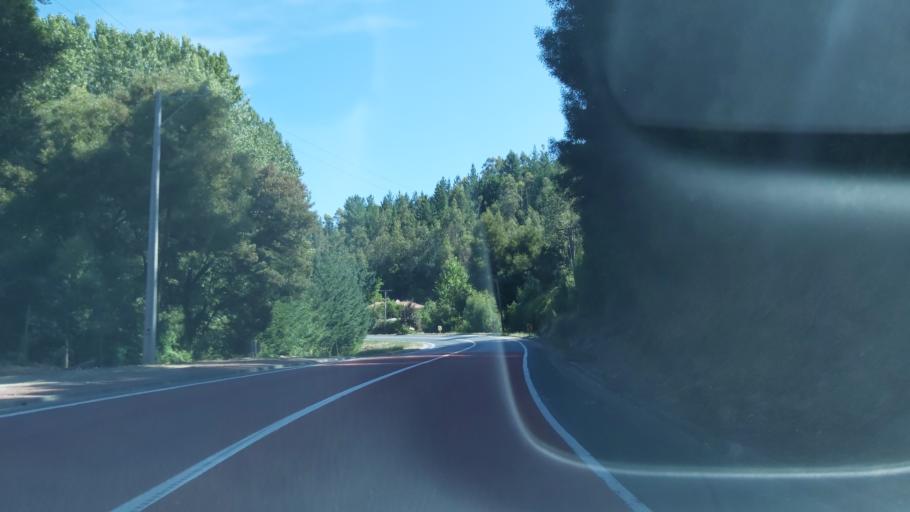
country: CL
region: Biobio
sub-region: Provincia de Concepcion
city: Lota
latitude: -37.1187
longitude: -72.9843
